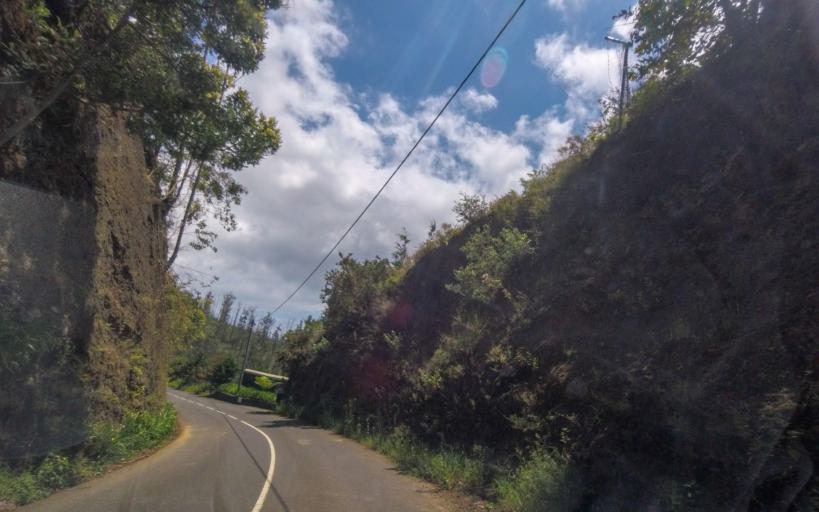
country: PT
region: Madeira
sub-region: Funchal
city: Nossa Senhora do Monte
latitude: 32.6807
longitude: -16.8838
